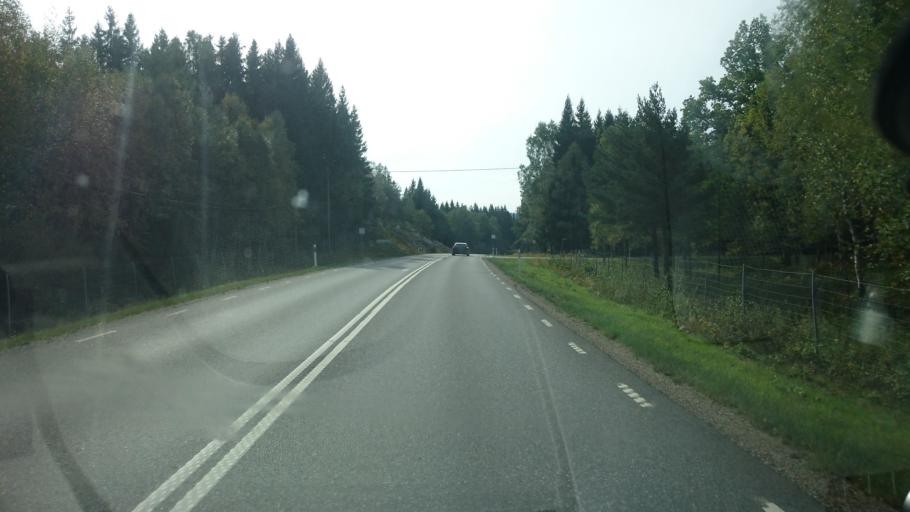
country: SE
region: Vaestra Goetaland
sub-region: Alingsas Kommun
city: Alingsas
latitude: 58.0010
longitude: 12.4441
